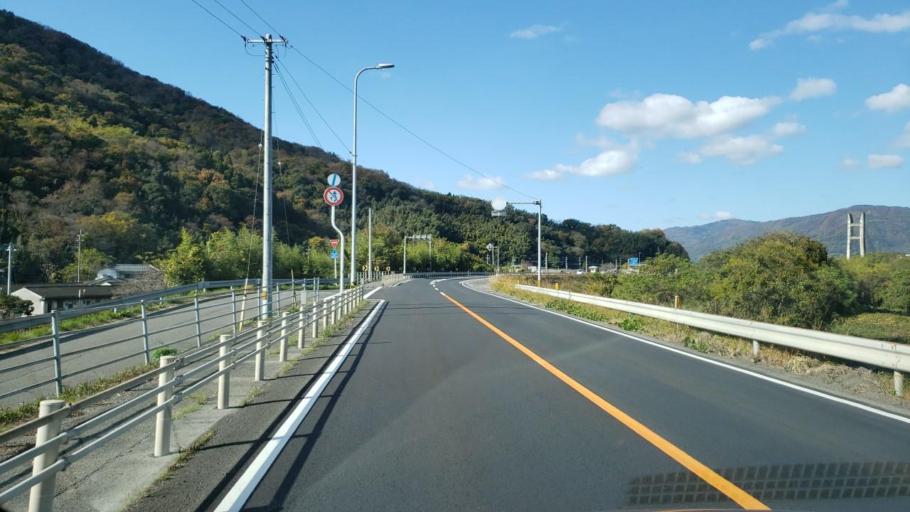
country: JP
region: Tokushima
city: Wakimachi
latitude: 34.0623
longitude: 134.2012
